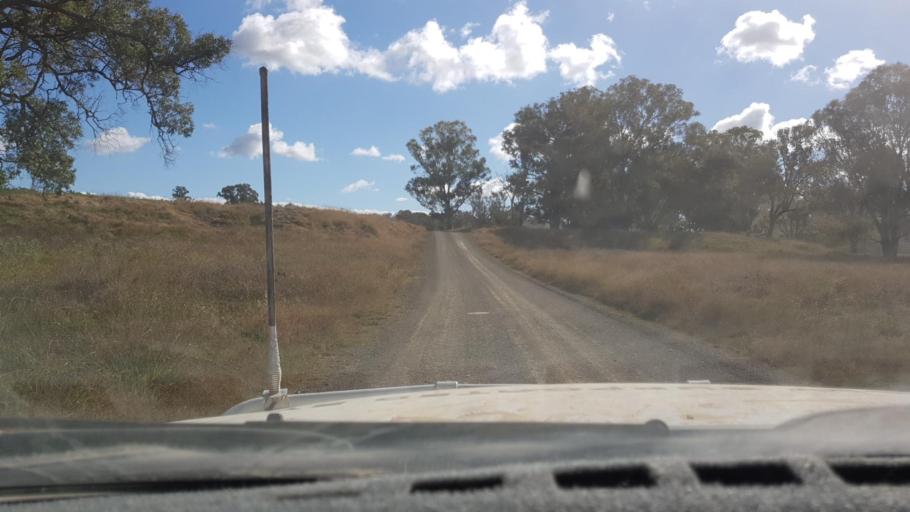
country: AU
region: New South Wales
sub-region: Narrabri
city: Blair Athol
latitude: -30.5745
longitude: 150.4716
